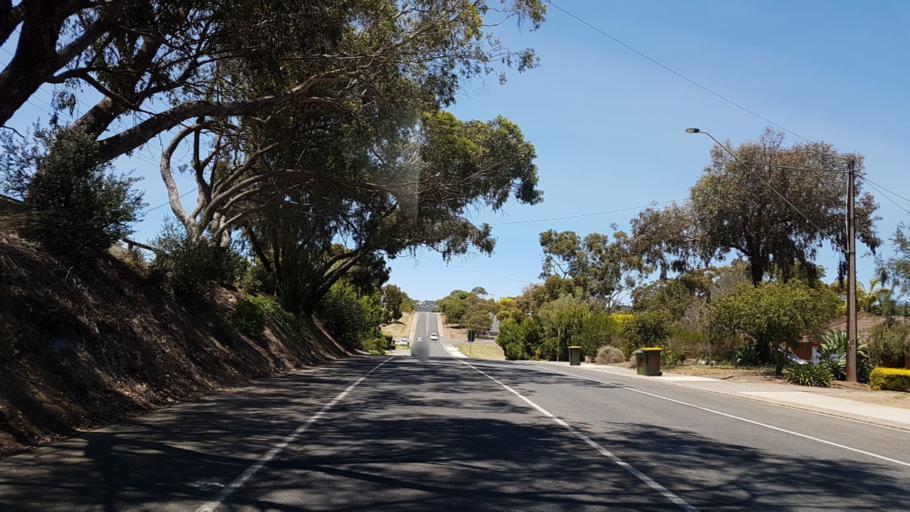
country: AU
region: South Australia
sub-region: Marion
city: Trott Park
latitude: -35.0829
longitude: 138.5529
